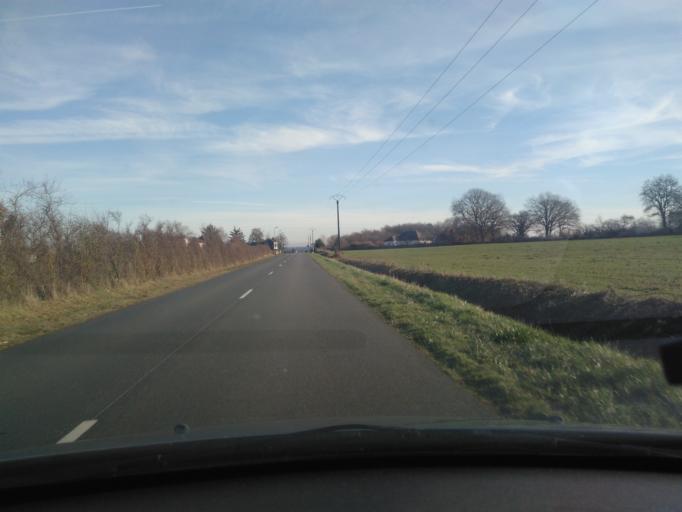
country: FR
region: Centre
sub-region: Departement du Cher
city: Le Chatelet
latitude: 46.6466
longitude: 2.3539
